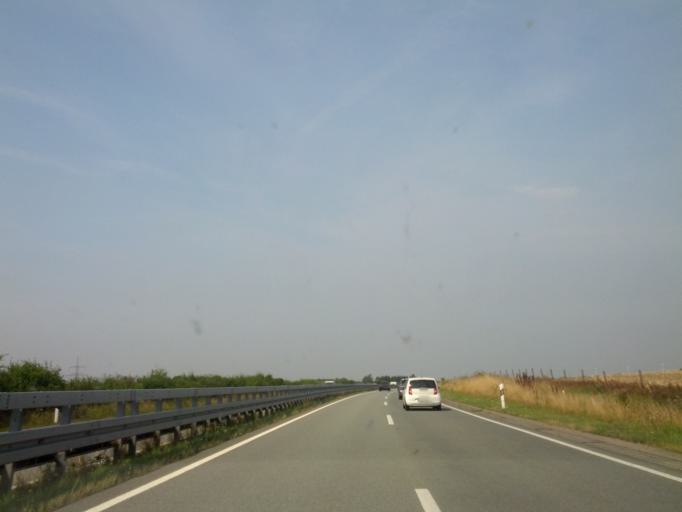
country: DE
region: Mecklenburg-Vorpommern
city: Brandshagen
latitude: 54.2064
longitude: 13.1524
